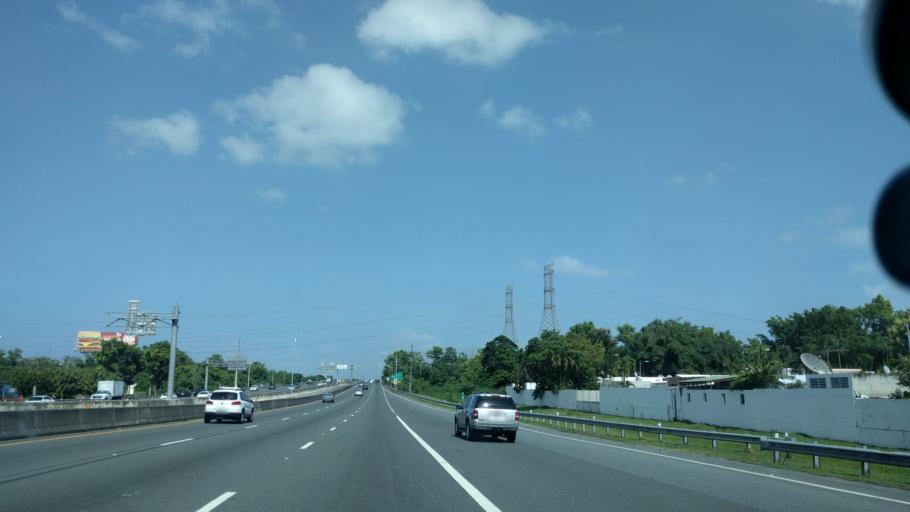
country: PR
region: Bayamon
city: Bayamon
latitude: 18.4210
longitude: -66.1612
